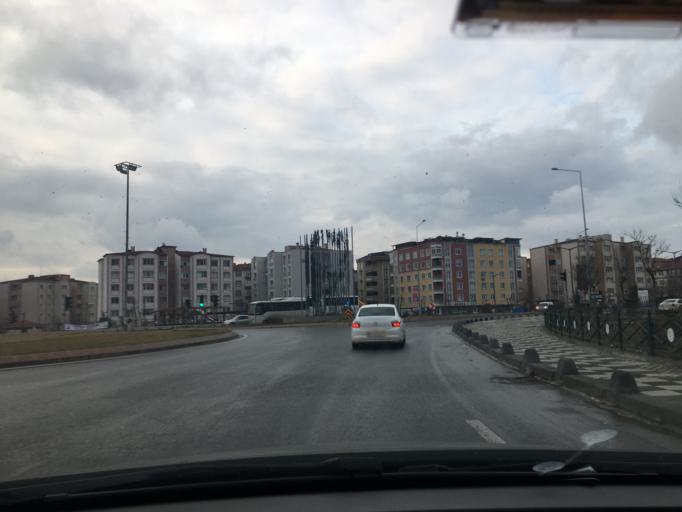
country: TR
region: Tekirdag
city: Cerkezkoey
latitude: 41.2801
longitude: 27.9821
